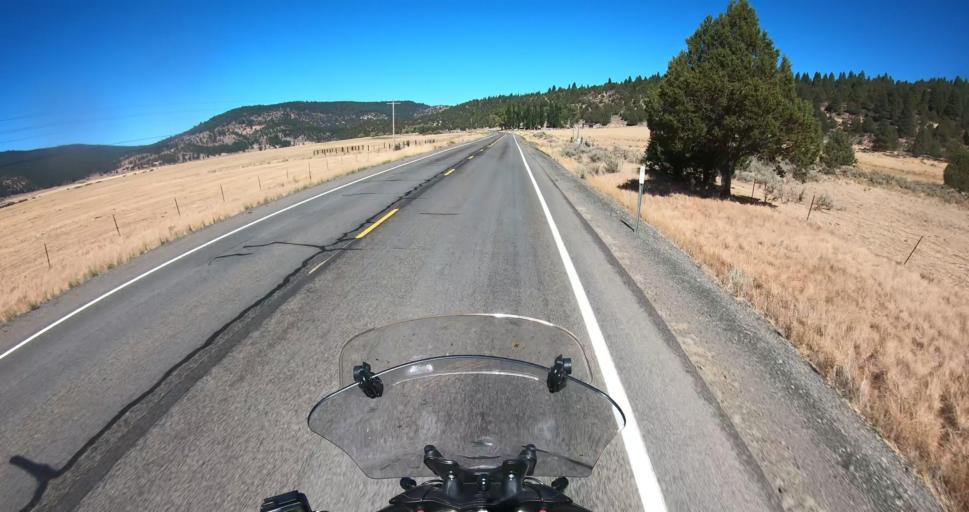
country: US
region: Oregon
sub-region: Lake County
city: Lakeview
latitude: 42.3677
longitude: -120.2968
